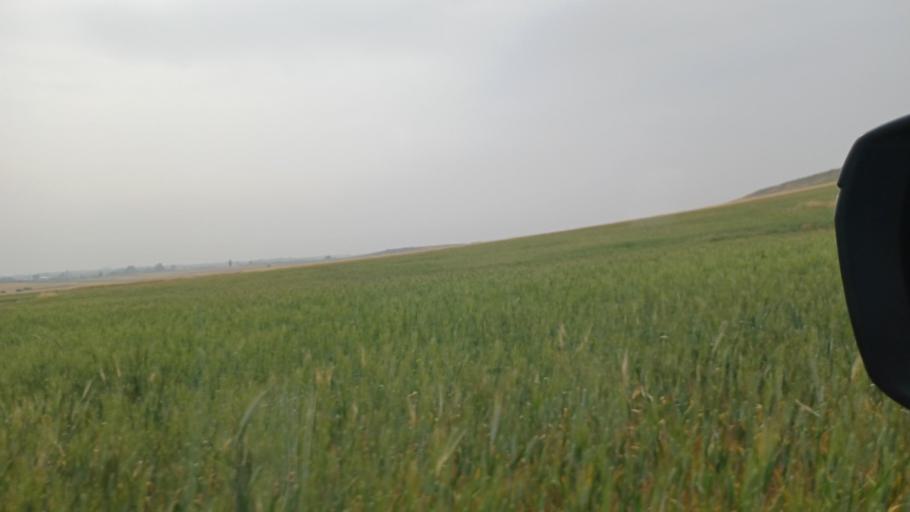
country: CY
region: Lefkosia
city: Mammari
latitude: 35.1677
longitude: 33.2338
